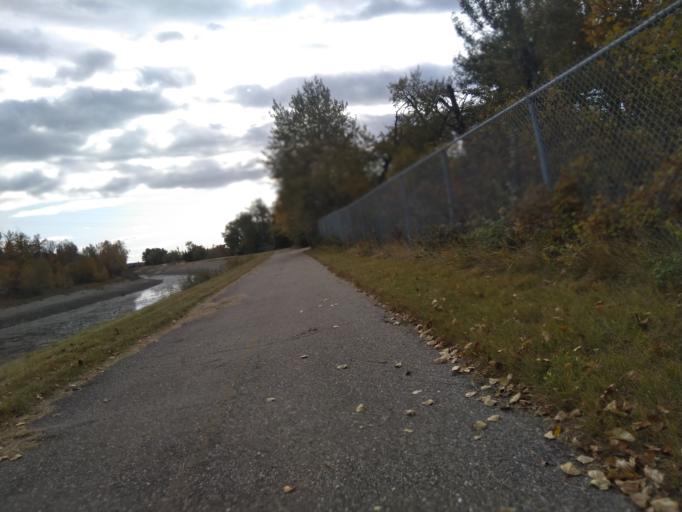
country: CA
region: Alberta
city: Calgary
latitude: 51.0186
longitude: -114.0082
